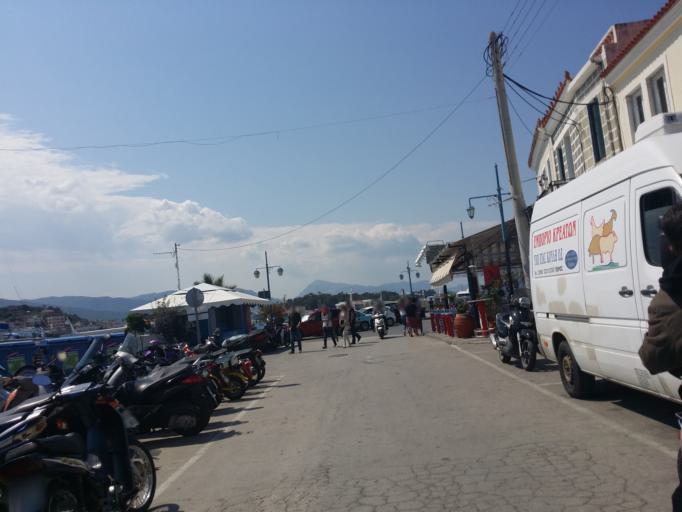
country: GR
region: Attica
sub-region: Nomos Piraios
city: Poros
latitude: 37.4984
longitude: 23.4527
